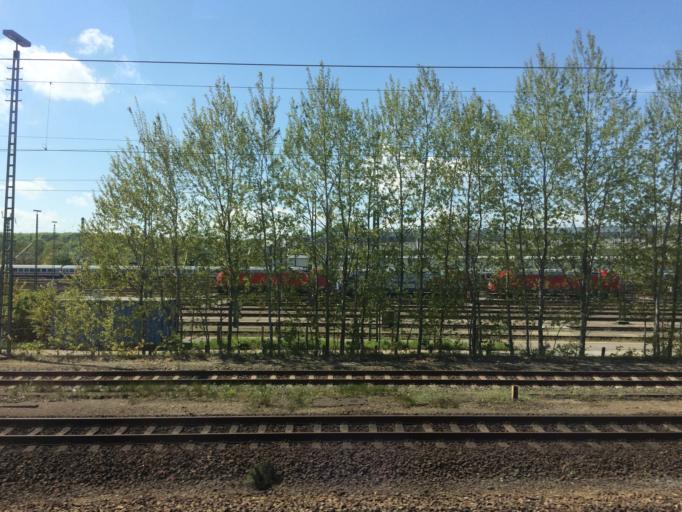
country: DE
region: Hamburg
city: Stellingen
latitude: 53.5879
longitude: 9.9195
